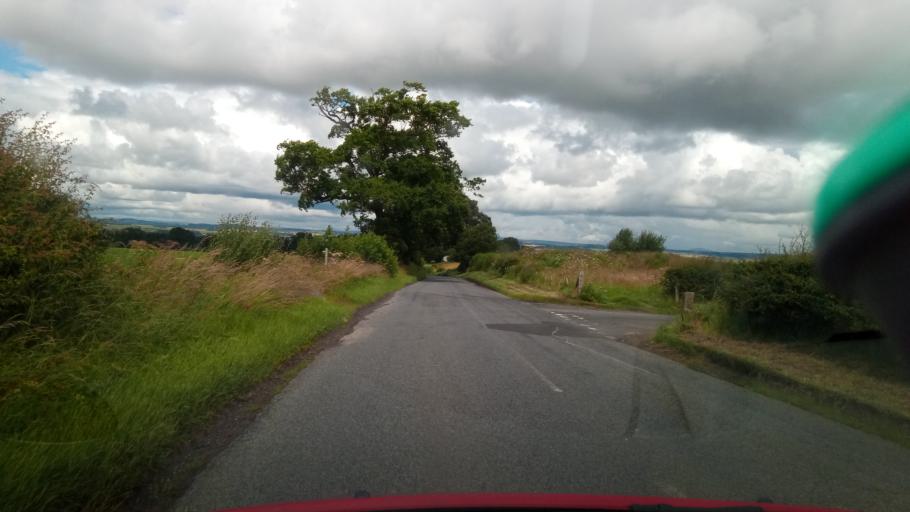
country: GB
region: Scotland
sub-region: The Scottish Borders
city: Kelso
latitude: 55.5673
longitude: -2.4169
